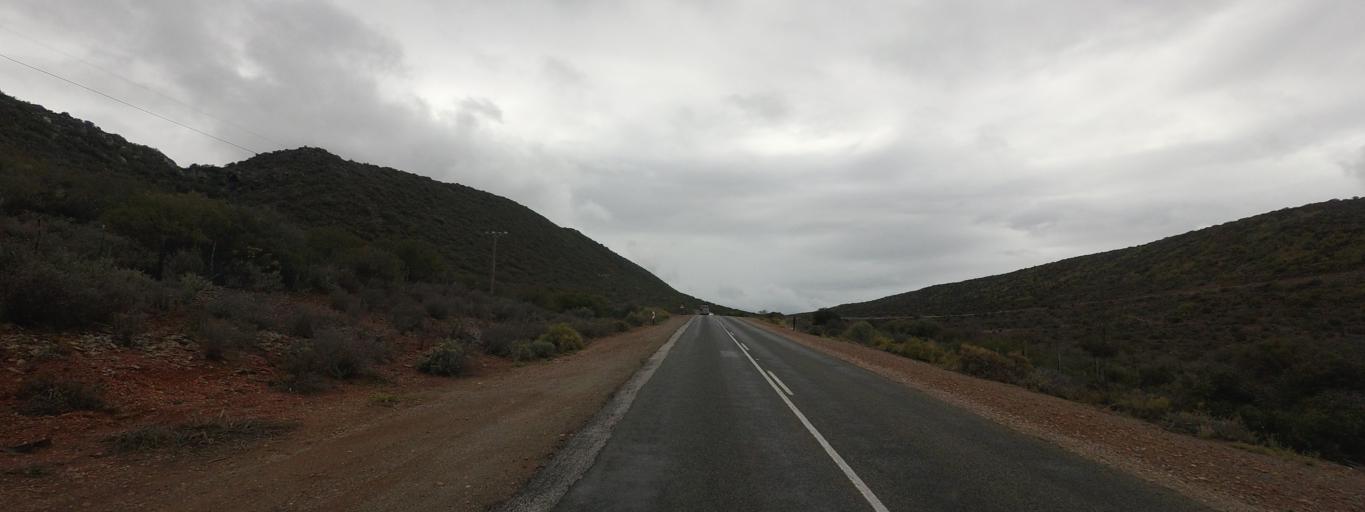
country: ZA
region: Western Cape
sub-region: Eden District Municipality
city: Oudtshoorn
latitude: -33.6840
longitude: 22.2693
